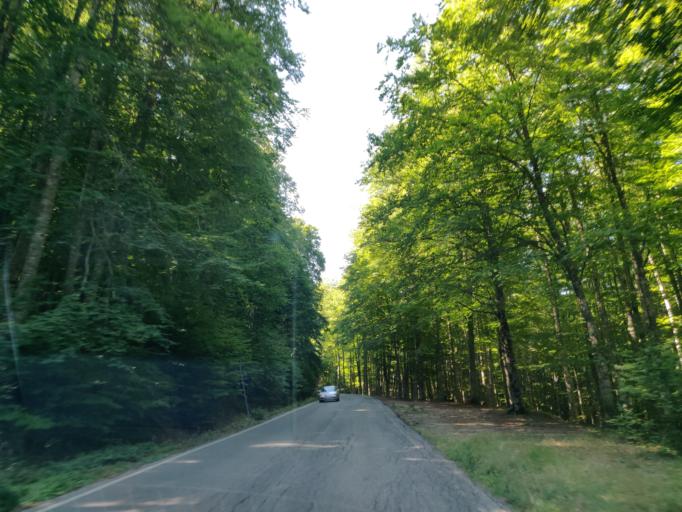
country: IT
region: Tuscany
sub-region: Provincia di Siena
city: Abbadia San Salvatore
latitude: 42.8969
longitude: 11.6136
